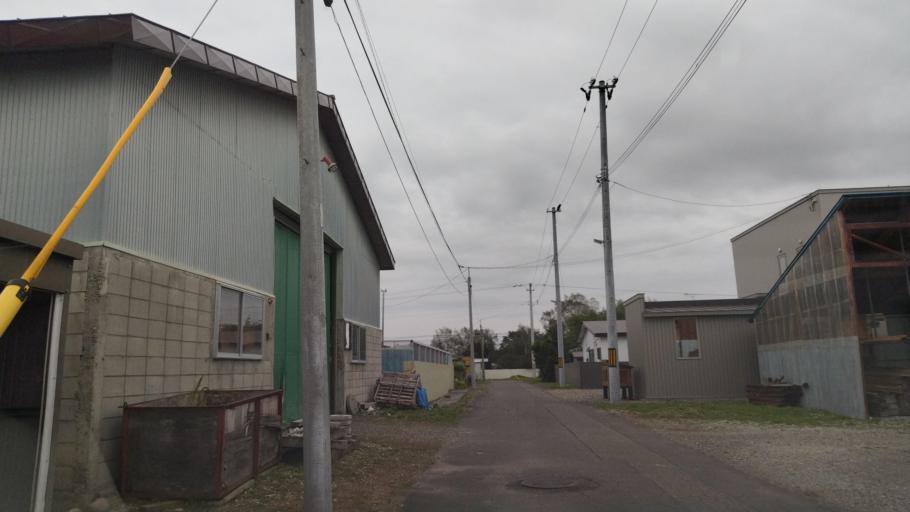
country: JP
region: Hokkaido
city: Otofuke
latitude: 43.2303
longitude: 143.2854
